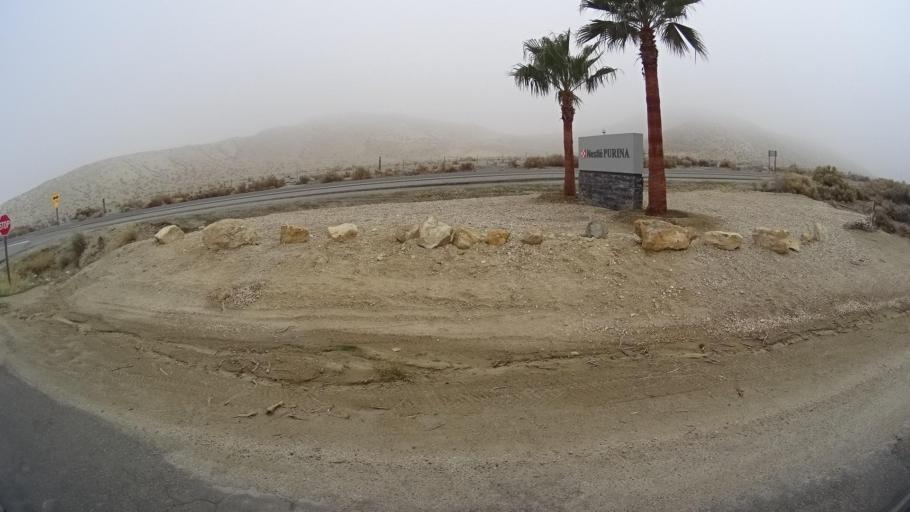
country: US
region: California
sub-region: Kern County
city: Maricopa
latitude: 35.0421
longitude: -119.4208
